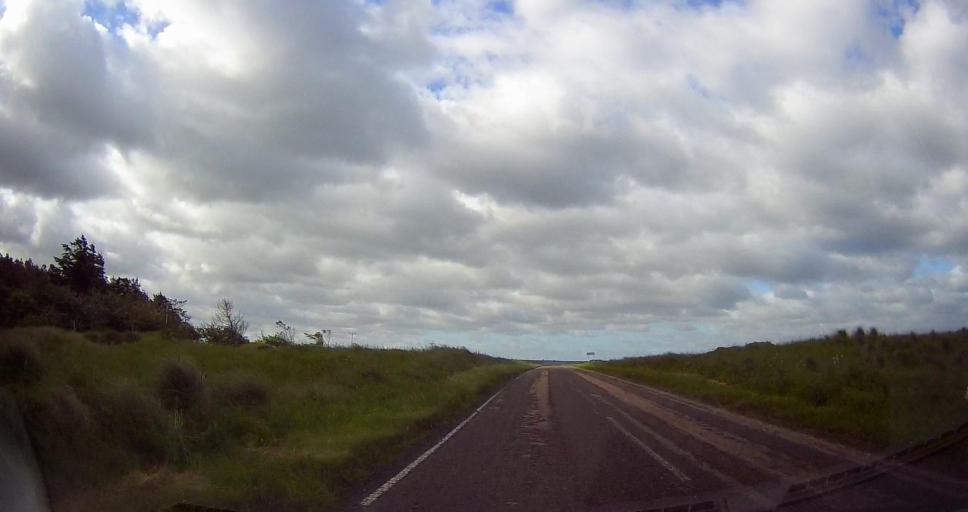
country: GB
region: Scotland
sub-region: Highland
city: Thurso
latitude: 58.6110
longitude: -3.3433
